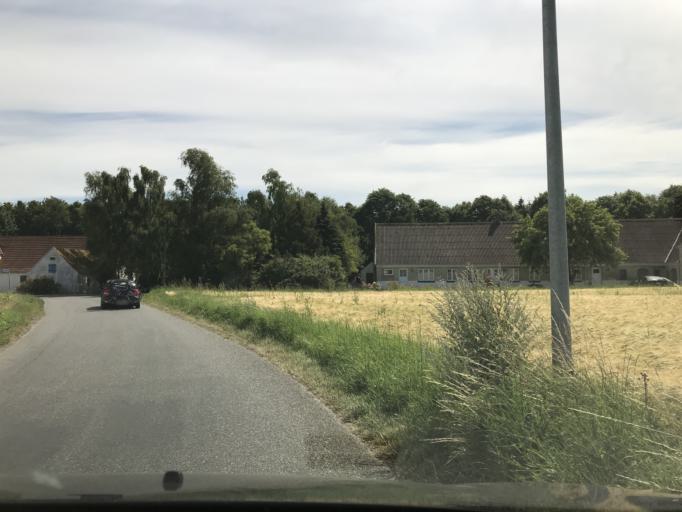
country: DK
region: South Denmark
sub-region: AEro Kommune
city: Marstal
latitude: 54.8483
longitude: 10.5111
